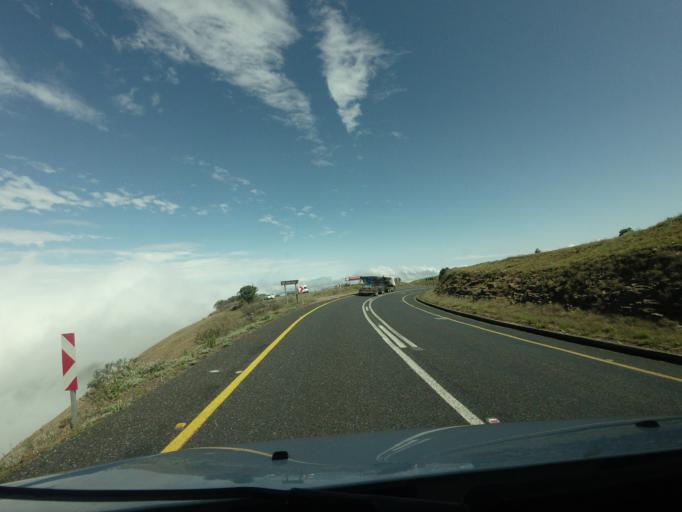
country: ZA
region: Mpumalanga
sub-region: Ehlanzeni District
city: Lydenburg
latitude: -25.1540
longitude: 30.6254
